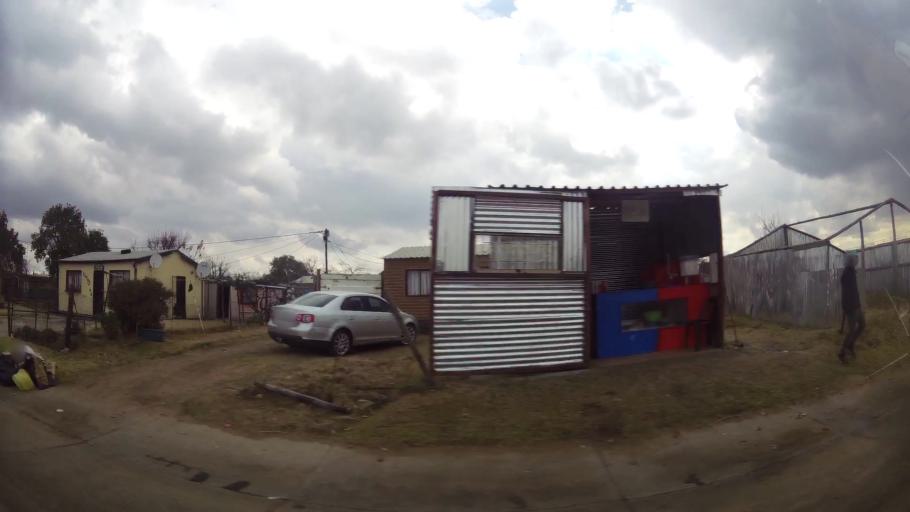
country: ZA
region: Orange Free State
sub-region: Fezile Dabi District Municipality
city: Sasolburg
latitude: -26.8495
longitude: 27.8781
